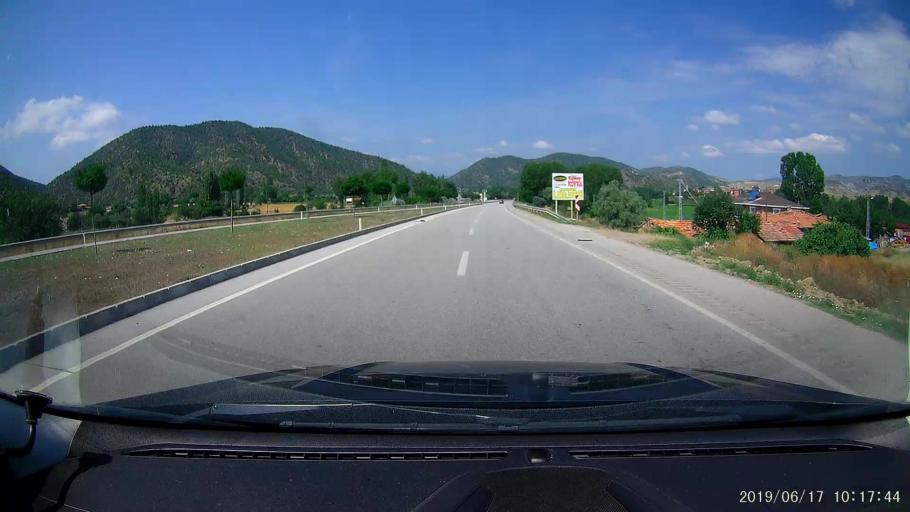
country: TR
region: Corum
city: Osmancik
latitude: 40.9790
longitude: 34.9408
